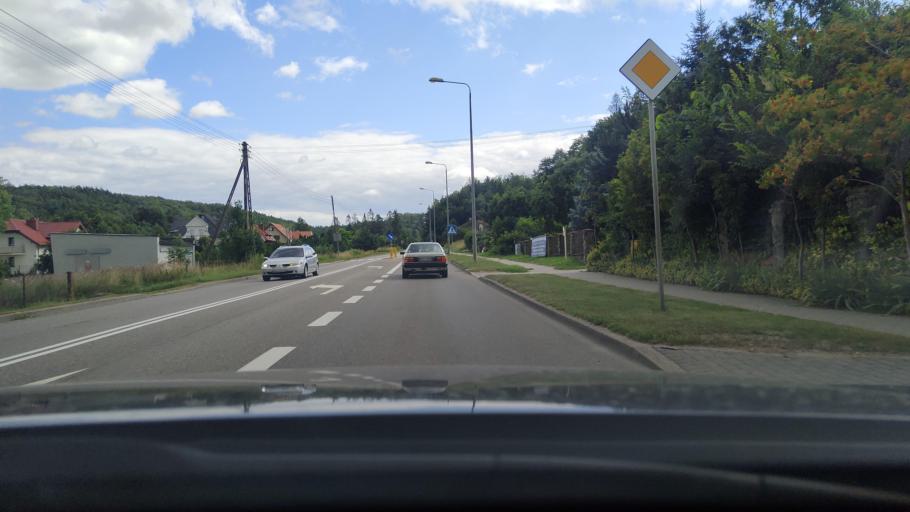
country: PL
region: Pomeranian Voivodeship
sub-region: Powiat wejherowski
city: Wejherowo
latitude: 54.5884
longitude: 18.2466
